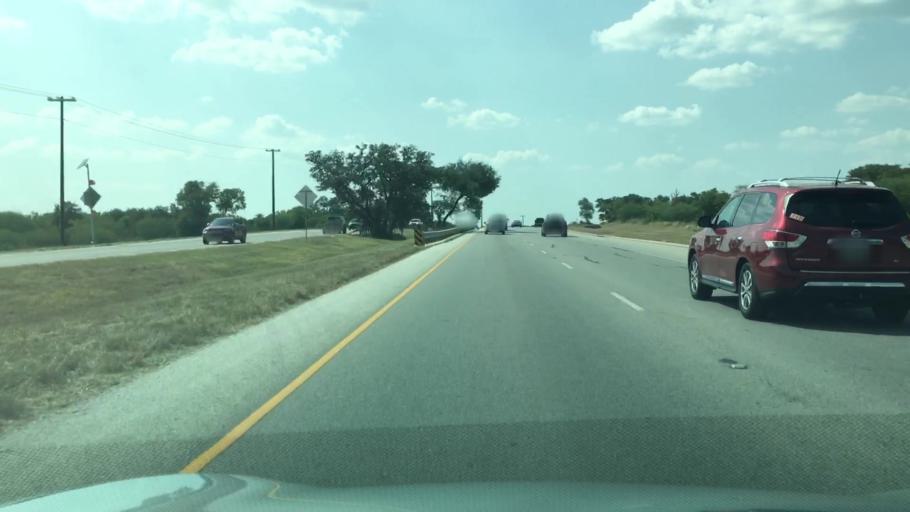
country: US
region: Texas
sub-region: Hays County
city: San Marcos
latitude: 29.8832
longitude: -97.9756
